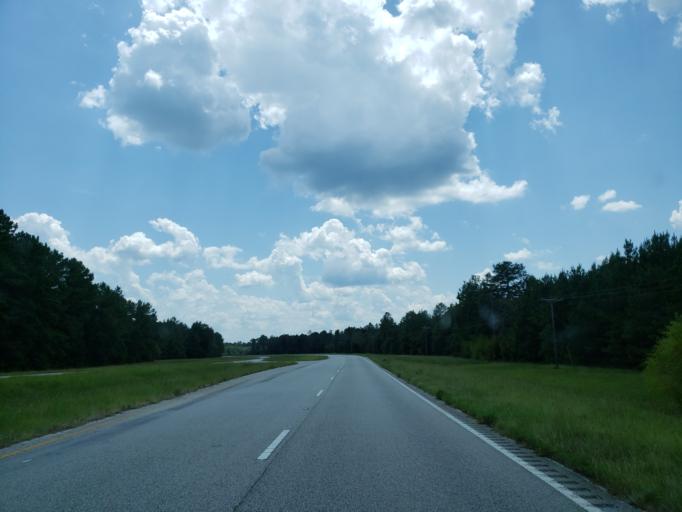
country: US
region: Mississippi
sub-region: Greene County
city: Leakesville
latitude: 31.2523
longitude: -88.5249
